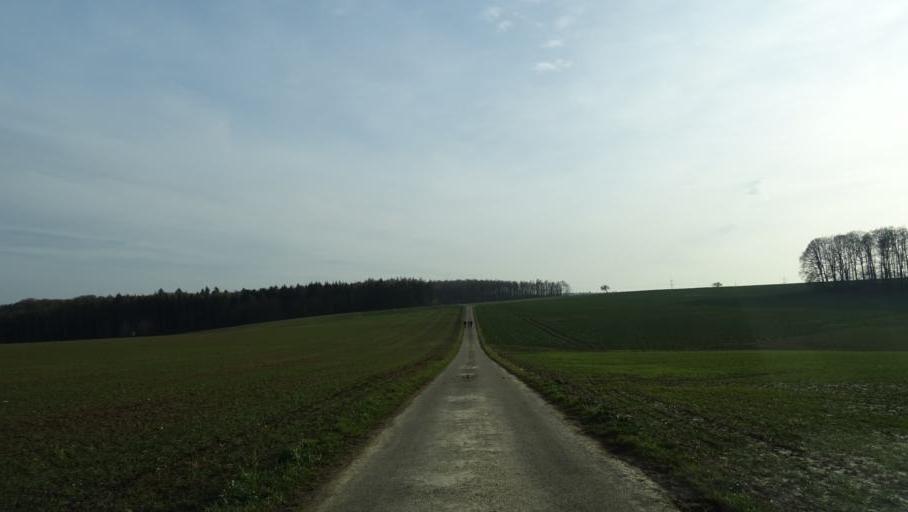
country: DE
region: Baden-Wuerttemberg
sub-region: Karlsruhe Region
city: Mosbach
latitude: 49.3580
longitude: 9.1913
